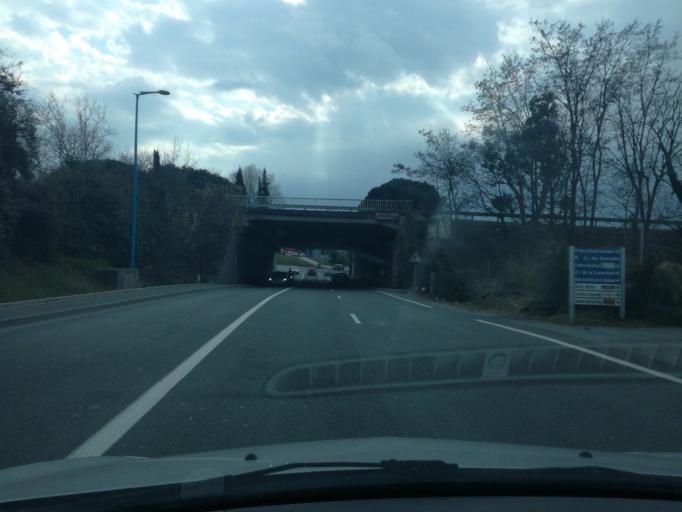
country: FR
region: Provence-Alpes-Cote d'Azur
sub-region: Departement des Alpes-Maritimes
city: Mandelieu-la-Napoule
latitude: 43.5586
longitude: 6.9515
